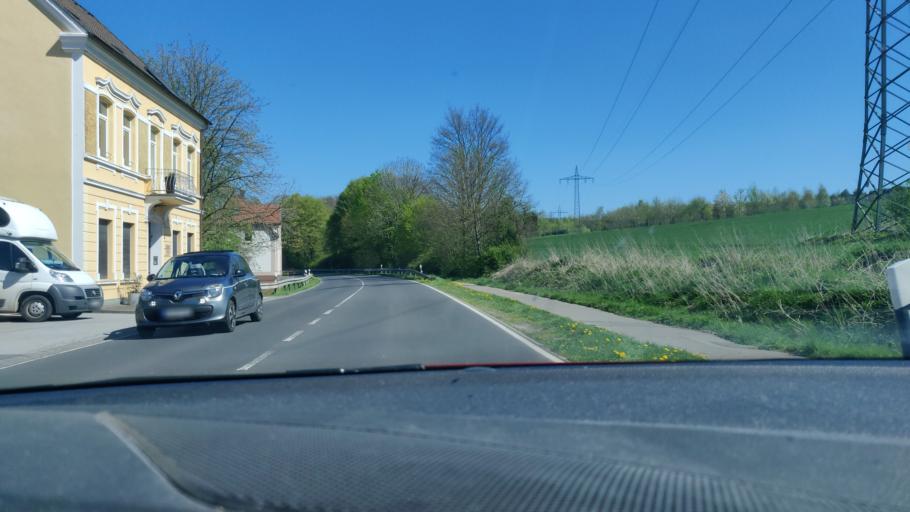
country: DE
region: North Rhine-Westphalia
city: Wulfrath
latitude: 51.2755
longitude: 7.0730
